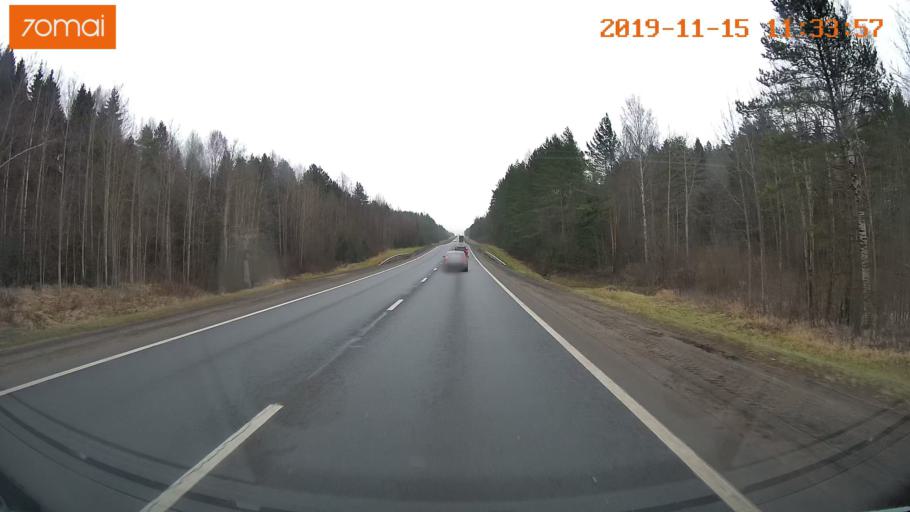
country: RU
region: Vologda
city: Molochnoye
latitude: 59.1913
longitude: 39.6017
